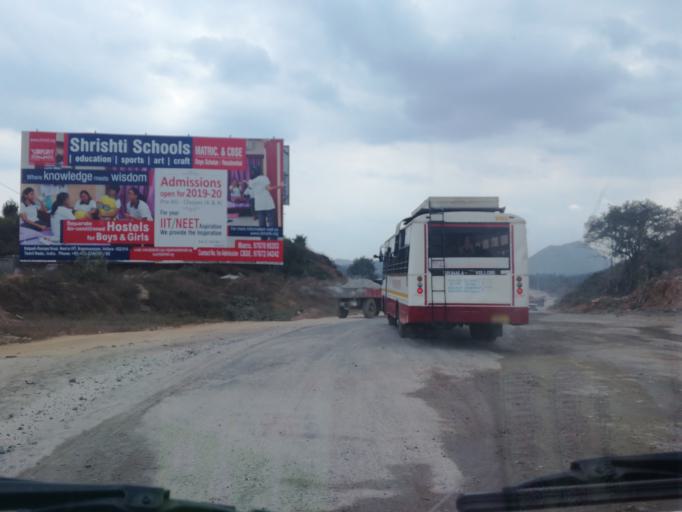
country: IN
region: Andhra Pradesh
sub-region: Chittoor
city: Ramapuram
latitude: 13.0872
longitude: 79.1354
